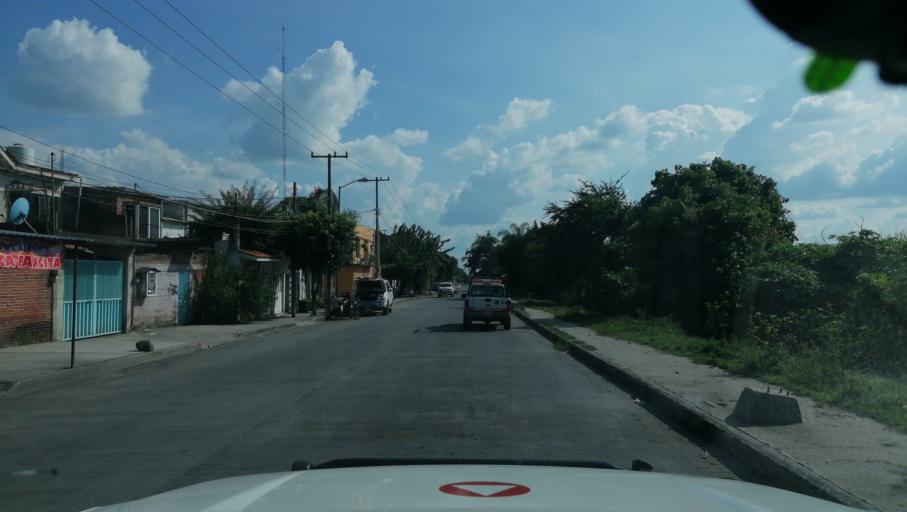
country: MX
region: Morelos
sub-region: Ayala
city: San Pedro Apatlaco
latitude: 18.8087
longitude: -98.9629
